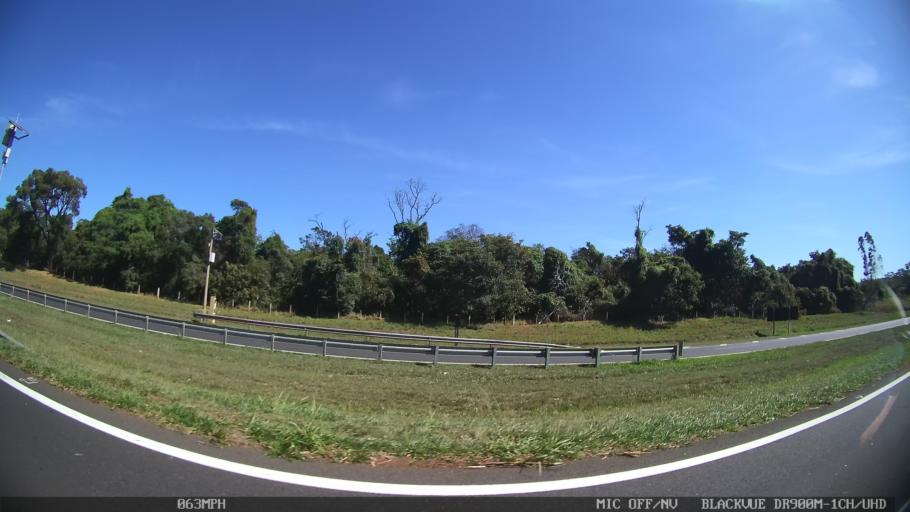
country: BR
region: Sao Paulo
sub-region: Sao Simao
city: Sao Simao
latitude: -21.5433
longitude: -47.6398
